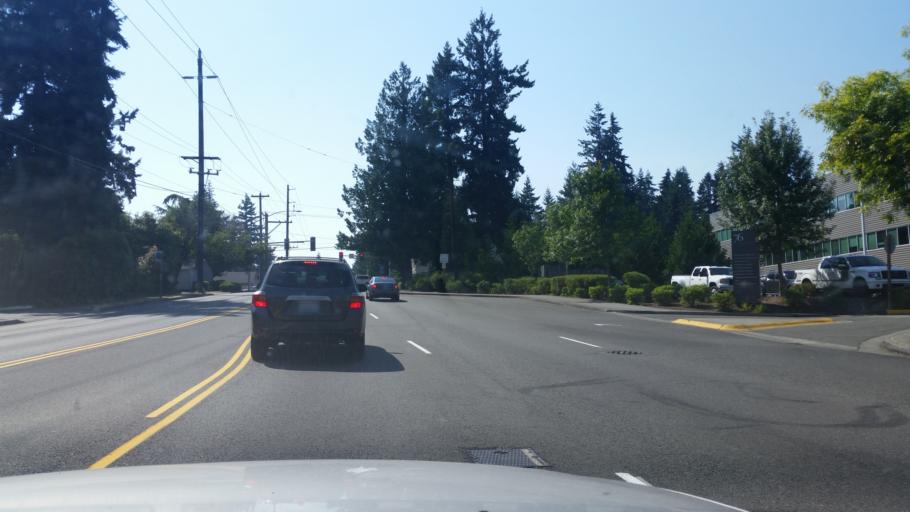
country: US
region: Washington
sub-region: Snohomish County
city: Esperance
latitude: 47.7997
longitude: -122.3342
